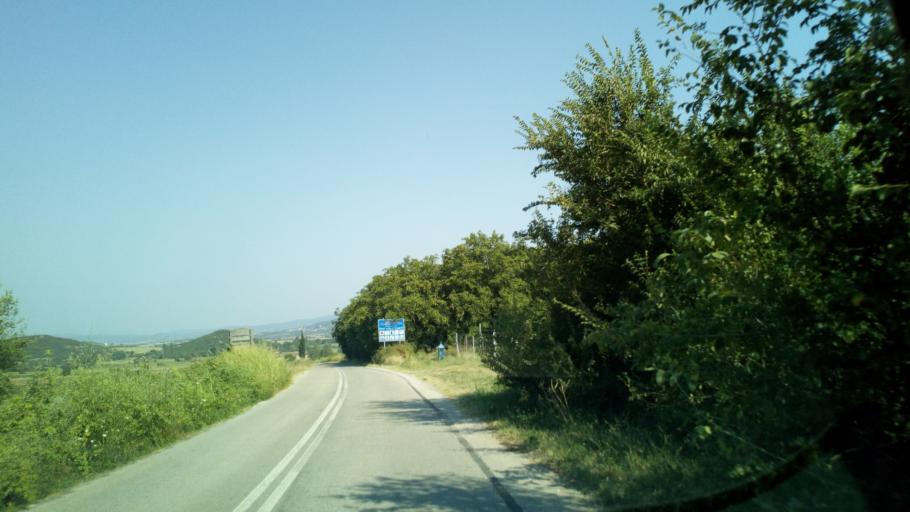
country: GR
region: Central Macedonia
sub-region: Nomos Chalkidikis
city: Galatista
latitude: 40.5125
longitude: 23.3638
